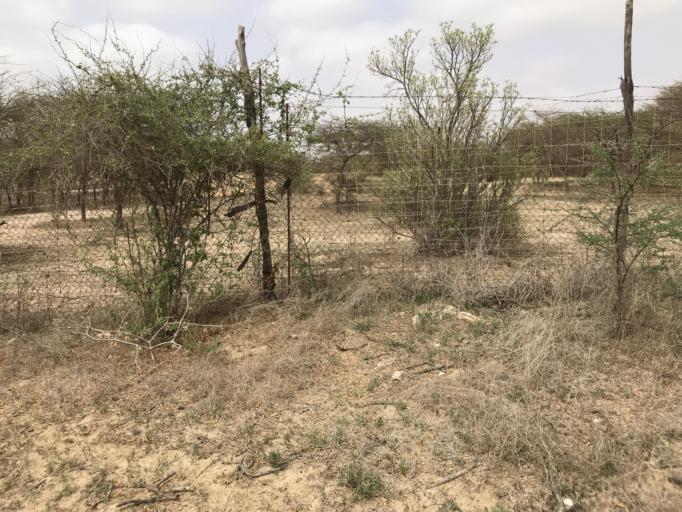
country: SN
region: Saint-Louis
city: Saint-Louis
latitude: 15.9251
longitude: -16.4539
